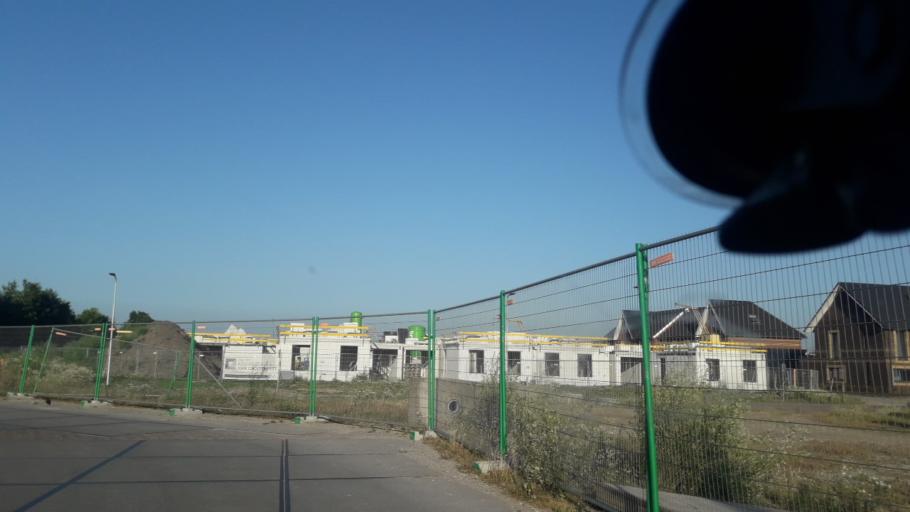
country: NL
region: Utrecht
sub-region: Gemeente Veenendaal
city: Veenendaal
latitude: 52.0205
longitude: 5.5821
